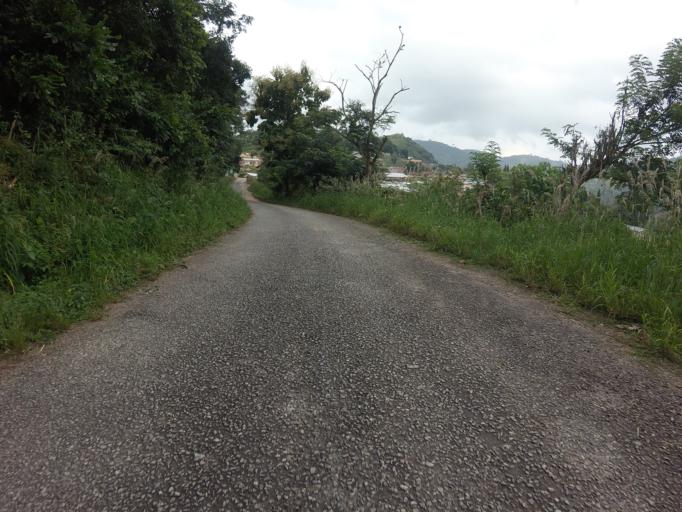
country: TG
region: Plateaux
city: Kpalime
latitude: 6.8892
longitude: 0.4523
